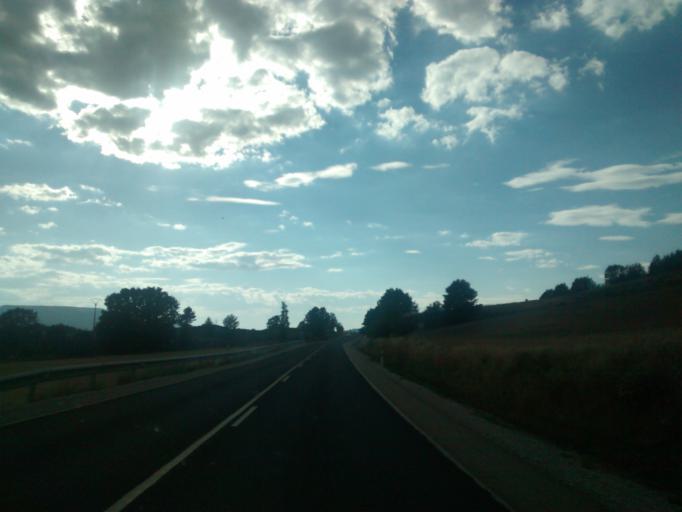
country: ES
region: Castille and Leon
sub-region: Provincia de Burgos
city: Basconcillos del Tozo
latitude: 42.6856
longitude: -3.9700
